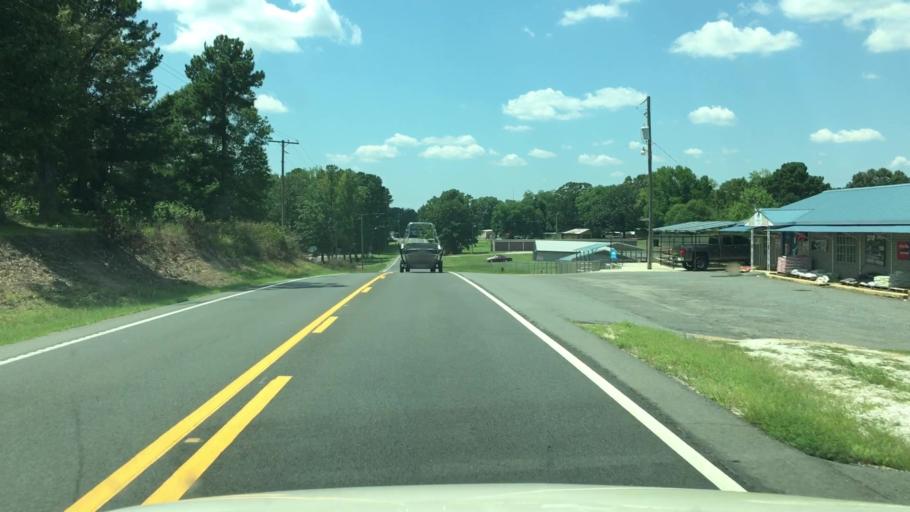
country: US
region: Arkansas
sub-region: Garland County
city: Lake Hamilton
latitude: 34.2663
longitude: -93.1391
